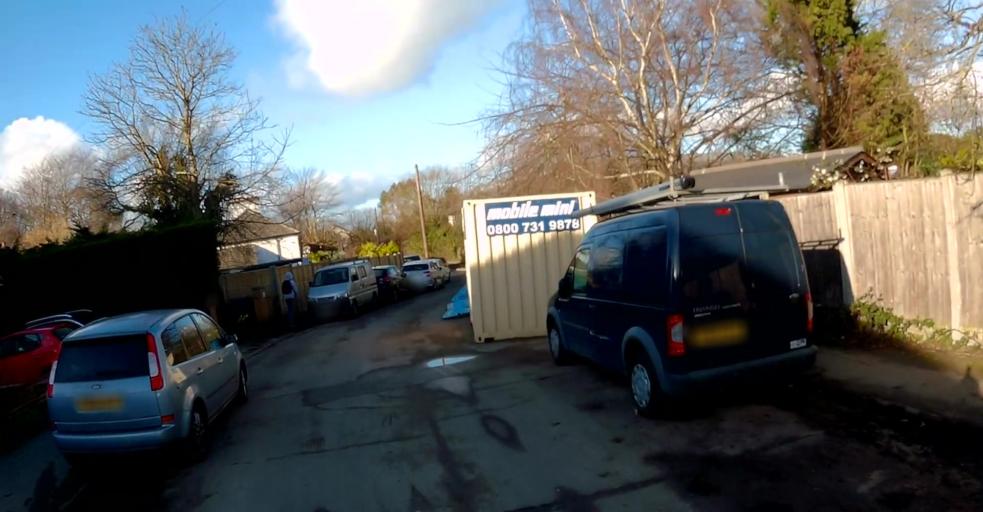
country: GB
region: England
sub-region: Surrey
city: Addlestone
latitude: 51.3711
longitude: -0.4793
